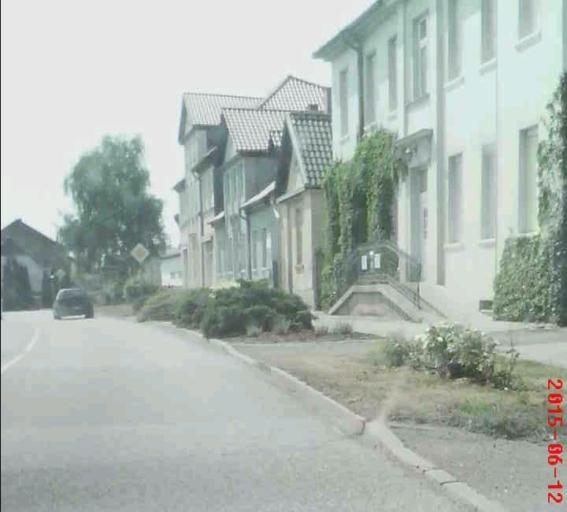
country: DE
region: Saxony-Anhalt
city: Rossla
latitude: 51.4635
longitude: 11.0790
